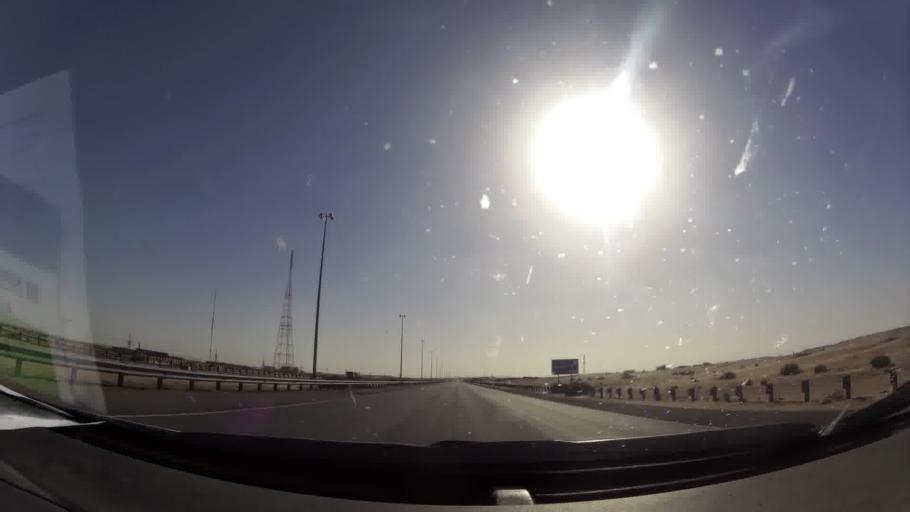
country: KW
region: Al Asimah
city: Kuwait City
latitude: 29.5973
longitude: 47.9104
